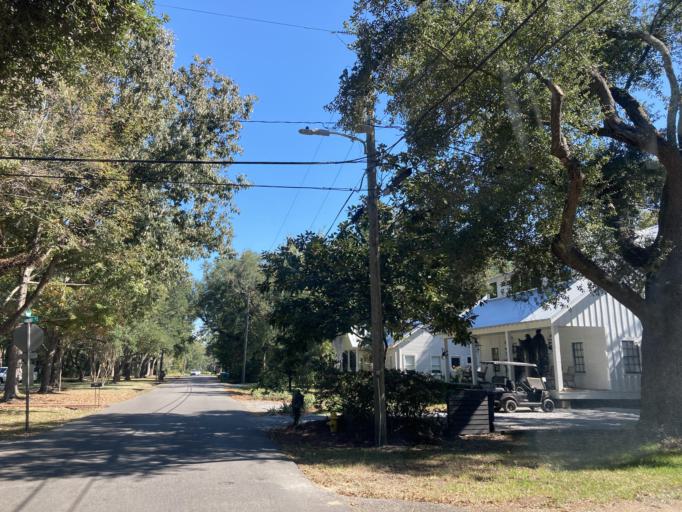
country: US
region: Mississippi
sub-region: Jackson County
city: Ocean Springs
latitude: 30.4115
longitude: -88.8369
